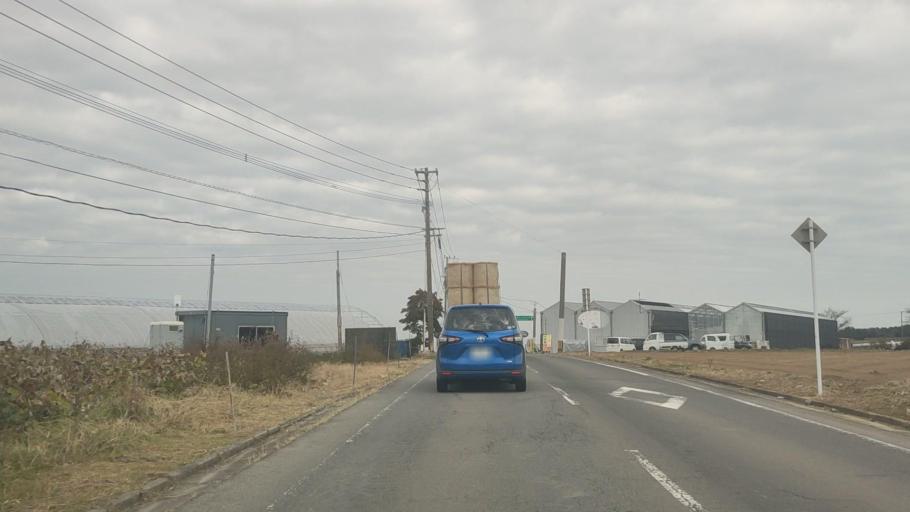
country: JP
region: Nagasaki
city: Shimabara
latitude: 32.8396
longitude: 130.2143
